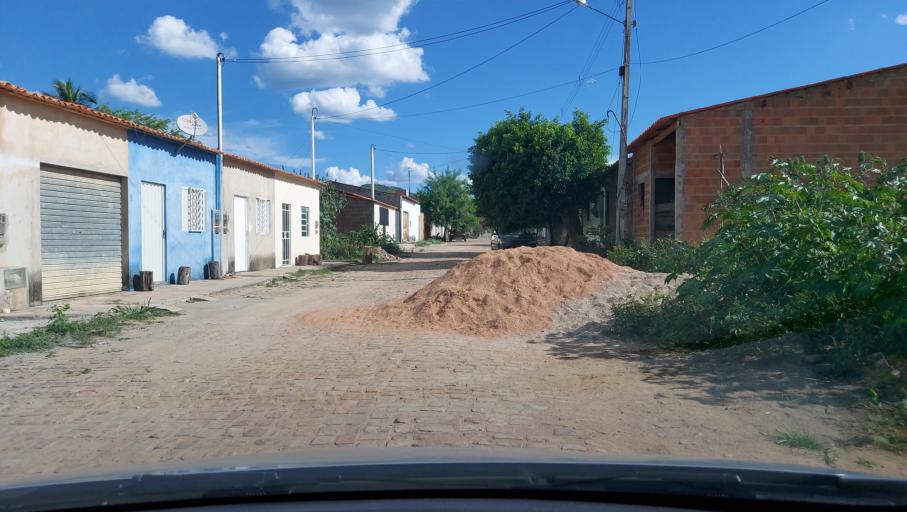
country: BR
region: Bahia
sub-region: Oliveira Dos Brejinhos
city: Beira Rio
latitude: -11.9964
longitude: -42.6270
